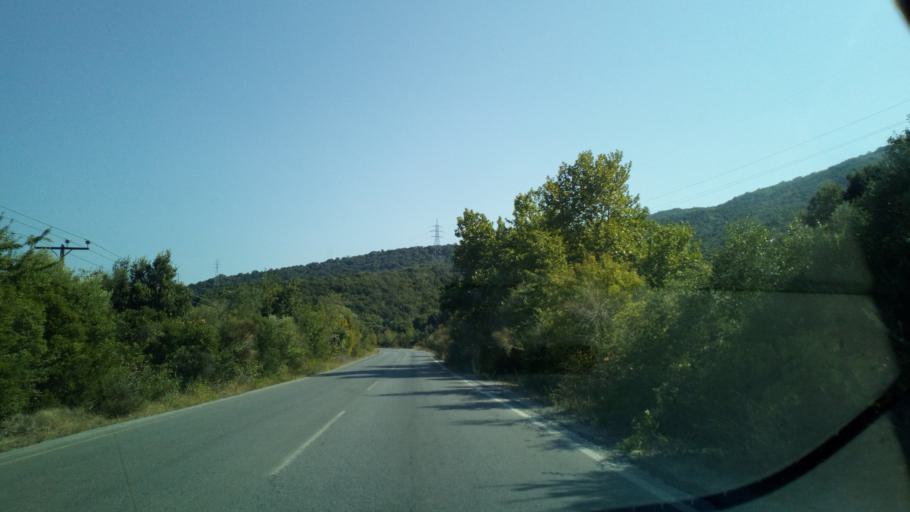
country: GR
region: Central Macedonia
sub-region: Nomos Thessalonikis
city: Stavros
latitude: 40.6392
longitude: 23.7507
